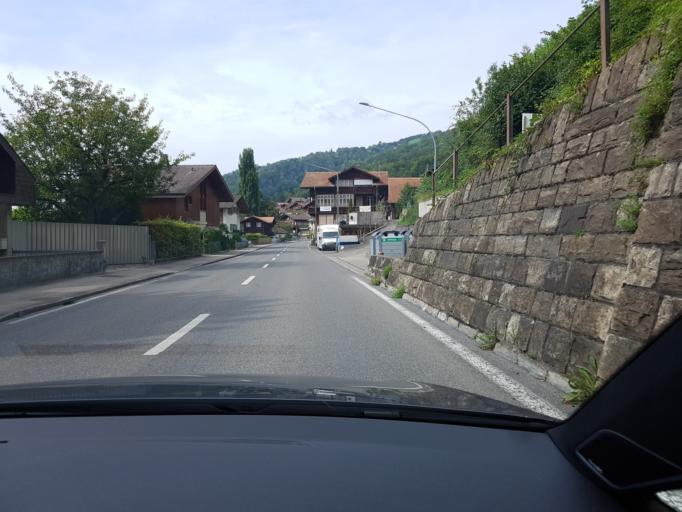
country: CH
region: Bern
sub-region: Thun District
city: Sigriswil
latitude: 46.6991
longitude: 7.7368
